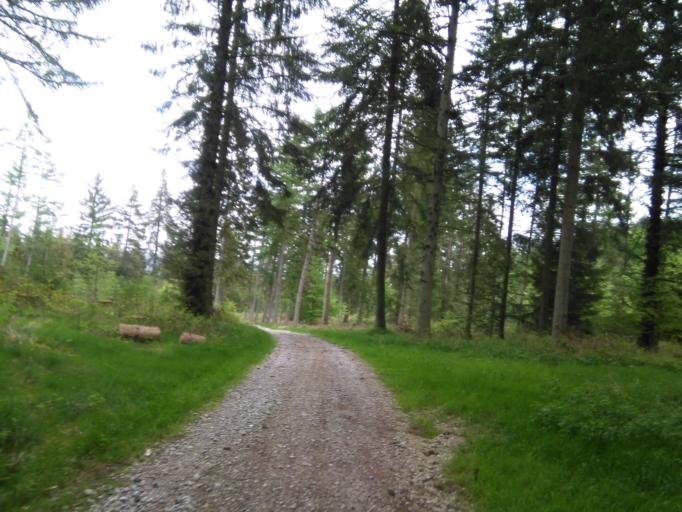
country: DK
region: Central Jutland
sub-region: Horsens Kommune
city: Braedstrup
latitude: 56.0496
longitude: 9.6273
